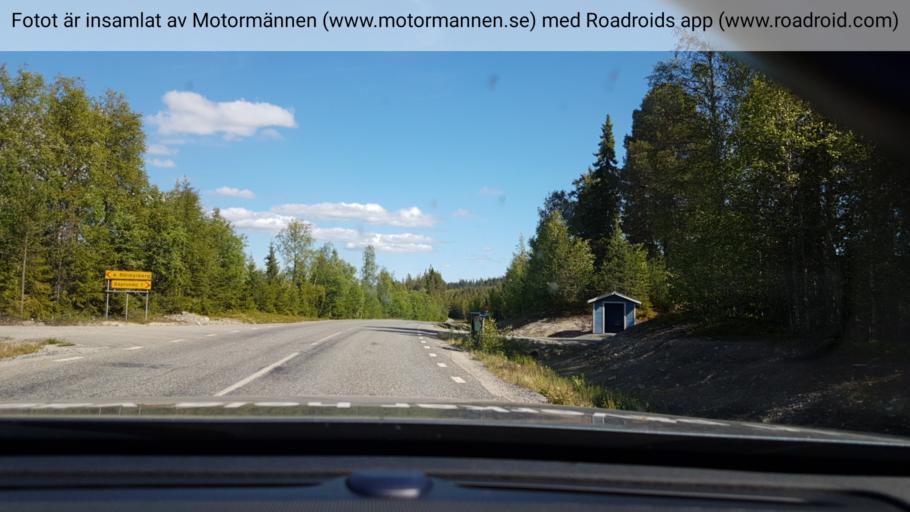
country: SE
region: Vaesterbotten
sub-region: Lycksele Kommun
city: Lycksele
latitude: 64.6235
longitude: 18.3951
